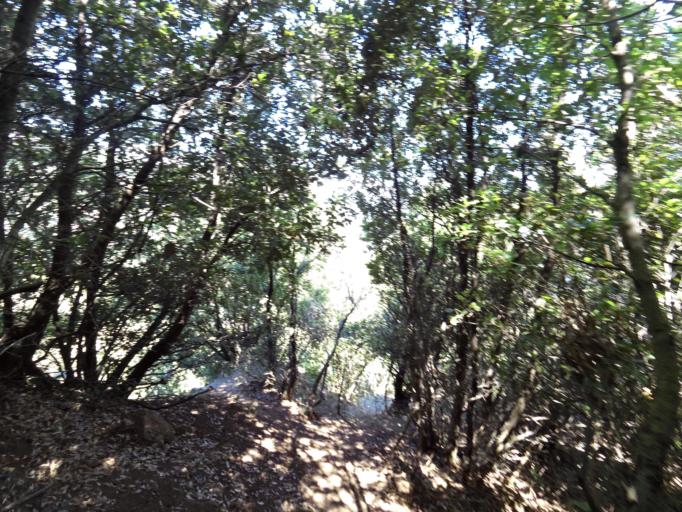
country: IT
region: Calabria
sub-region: Provincia di Reggio Calabria
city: Pazzano
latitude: 38.4633
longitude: 16.4294
